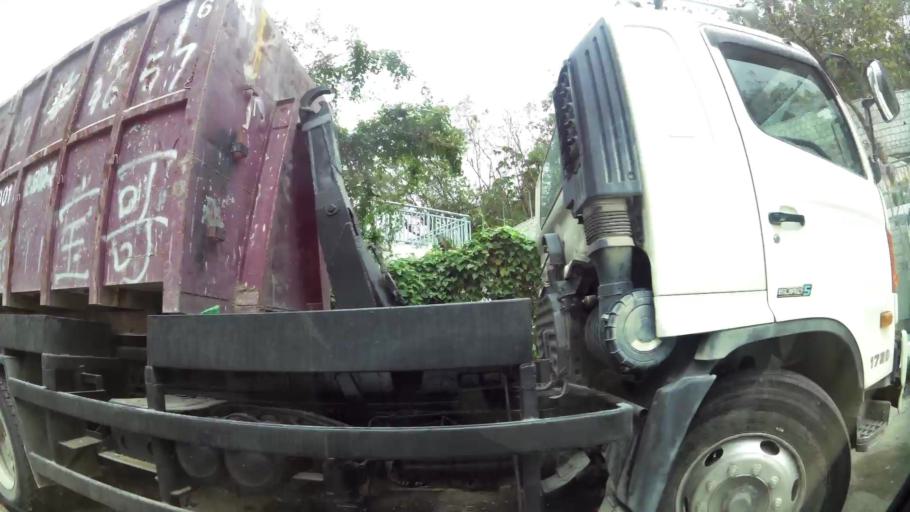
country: HK
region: Central and Western
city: Central
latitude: 22.2561
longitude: 114.1343
